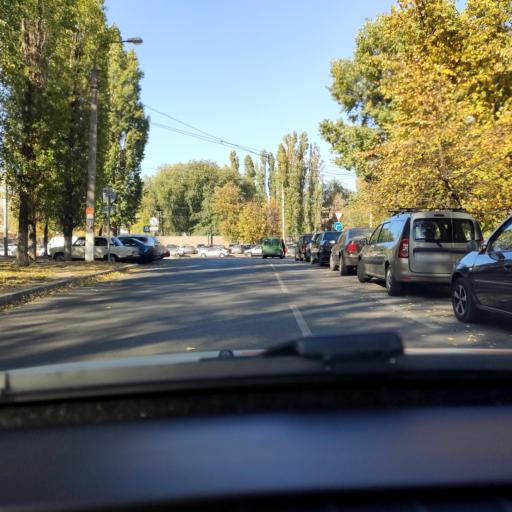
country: RU
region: Voronezj
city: Voronezh
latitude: 51.6514
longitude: 39.1690
